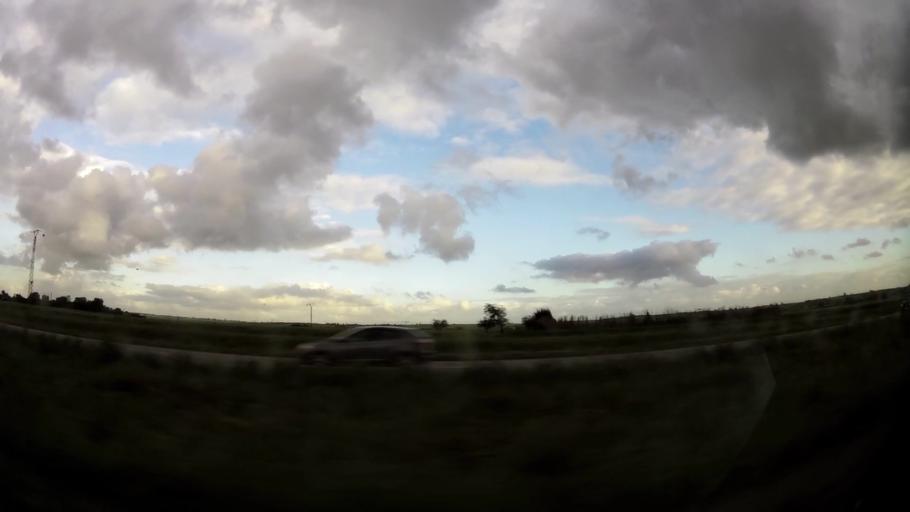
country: MA
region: Grand Casablanca
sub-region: Mediouna
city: Tit Mellil
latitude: 33.5952
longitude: -7.4448
